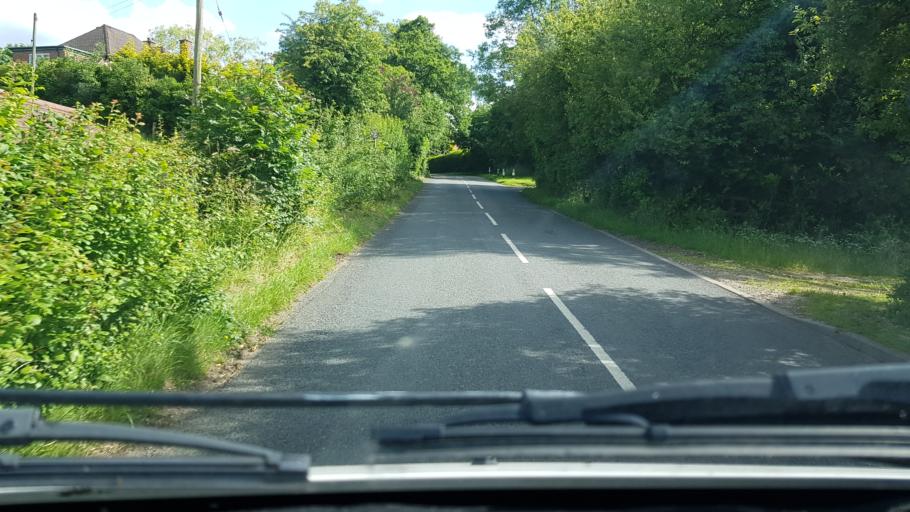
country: GB
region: England
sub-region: Shropshire
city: Romsley
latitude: 52.4261
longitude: -2.3076
